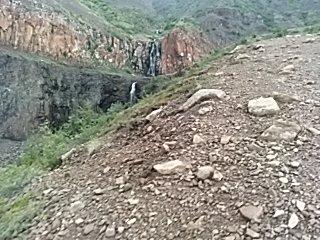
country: RU
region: Krasnoyarskiy
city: Talnakh
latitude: 69.4797
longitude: 88.5318
